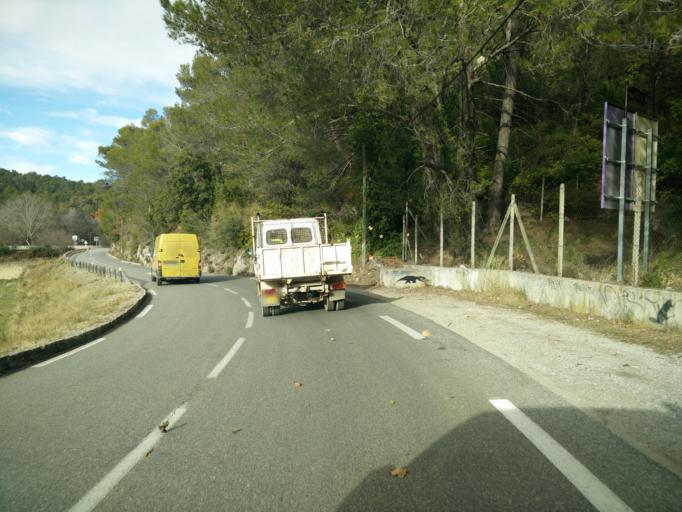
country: FR
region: Provence-Alpes-Cote d'Azur
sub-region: Departement du Var
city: Cotignac
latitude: 43.5337
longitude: 6.1465
